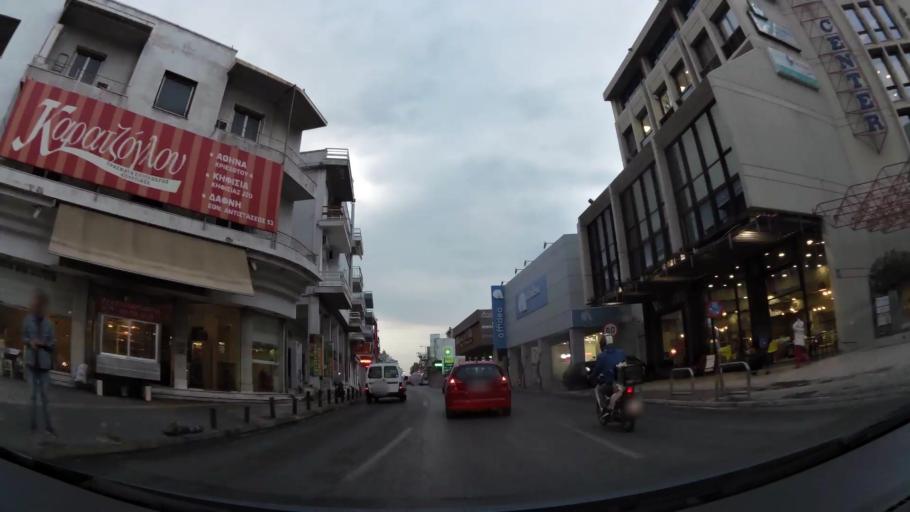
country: GR
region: Attica
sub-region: Nomarchia Athinas
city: Dhafni
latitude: 37.9486
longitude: 23.7385
